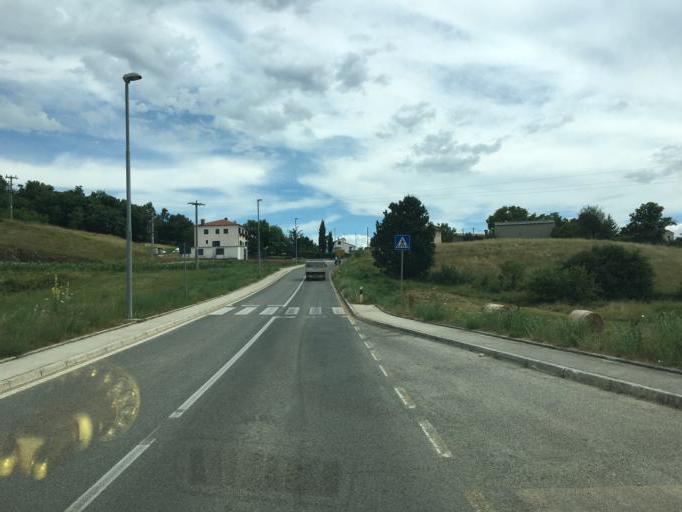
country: HR
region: Istarska
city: Karojba
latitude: 45.2601
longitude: 13.8713
